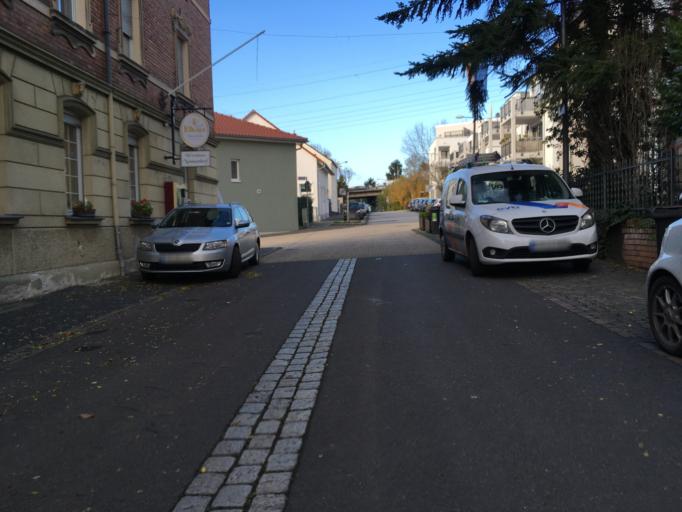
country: DE
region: Hesse
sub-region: Regierungsbezirk Darmstadt
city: Wiesbaden
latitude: 50.0512
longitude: 8.2383
